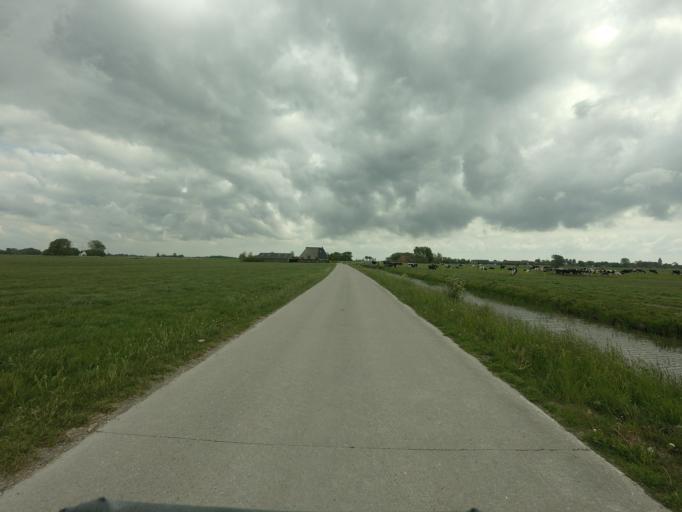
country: NL
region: Friesland
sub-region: Gemeente Littenseradiel
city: Wommels
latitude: 53.1084
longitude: 5.6161
